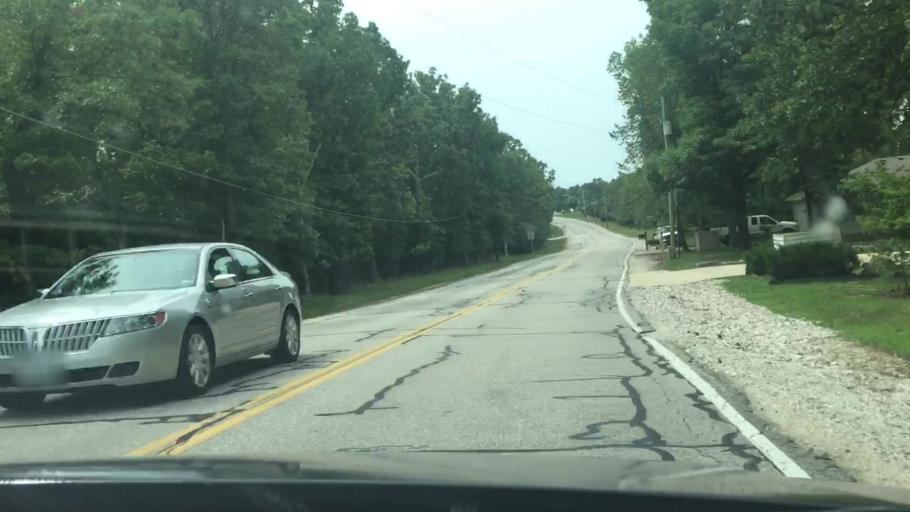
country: US
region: Missouri
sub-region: Camden County
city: Four Seasons
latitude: 38.2049
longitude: -92.7020
